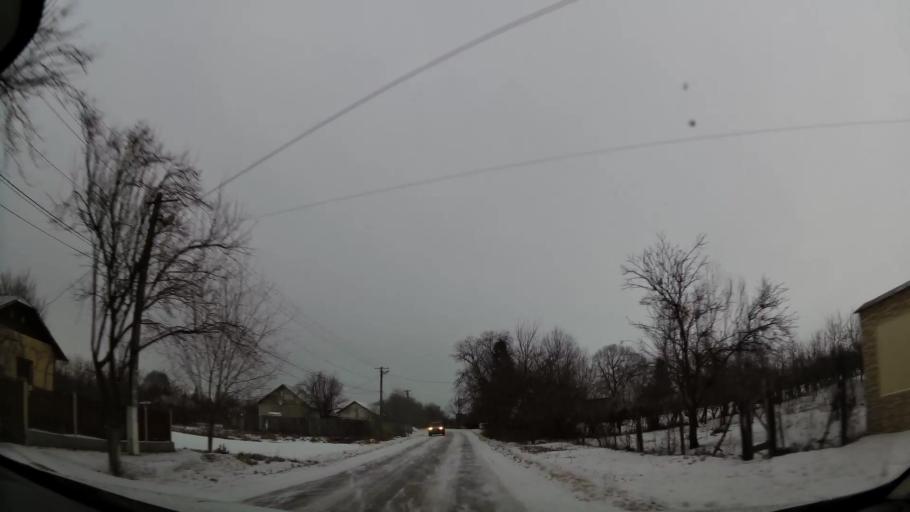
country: RO
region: Prahova
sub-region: Comuna Poenarii-Burchi
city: Ologeni
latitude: 44.7325
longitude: 25.9225
